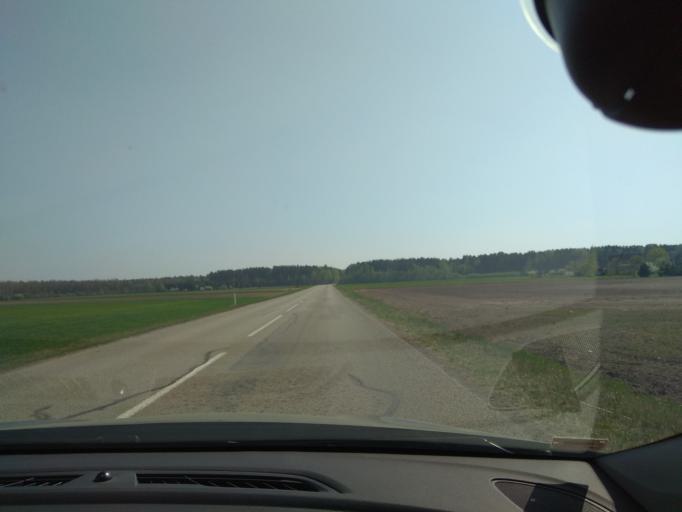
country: LT
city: Linkuva
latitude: 56.0017
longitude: 24.1639
